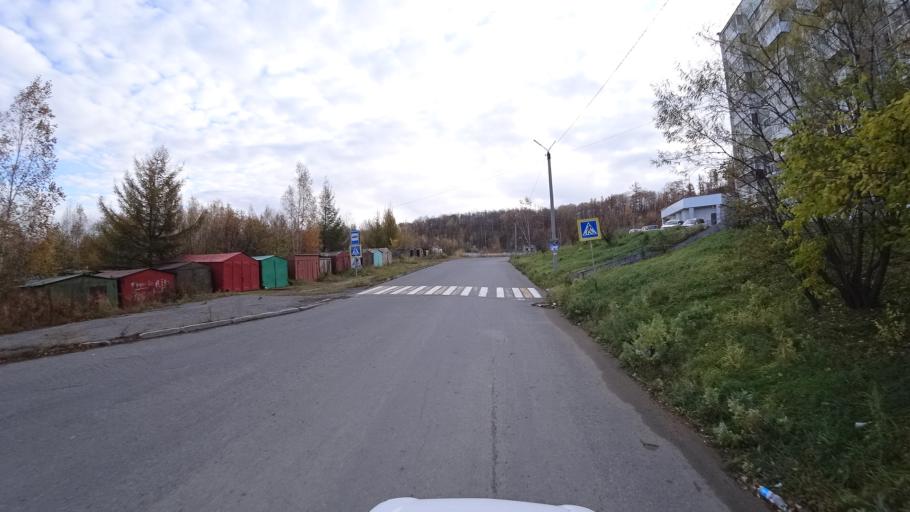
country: RU
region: Khabarovsk Krai
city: Amursk
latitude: 50.2488
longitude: 136.9217
